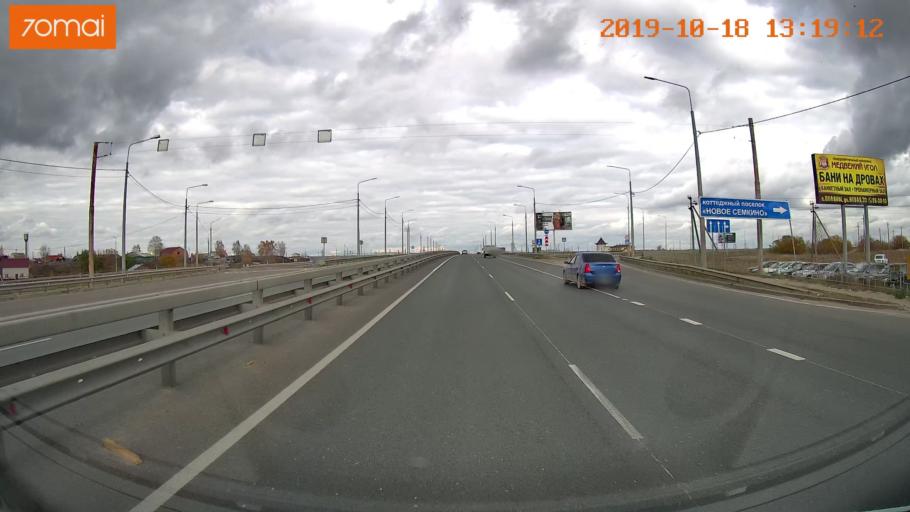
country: RU
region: Rjazan
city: Polyany
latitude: 54.6644
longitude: 39.8235
